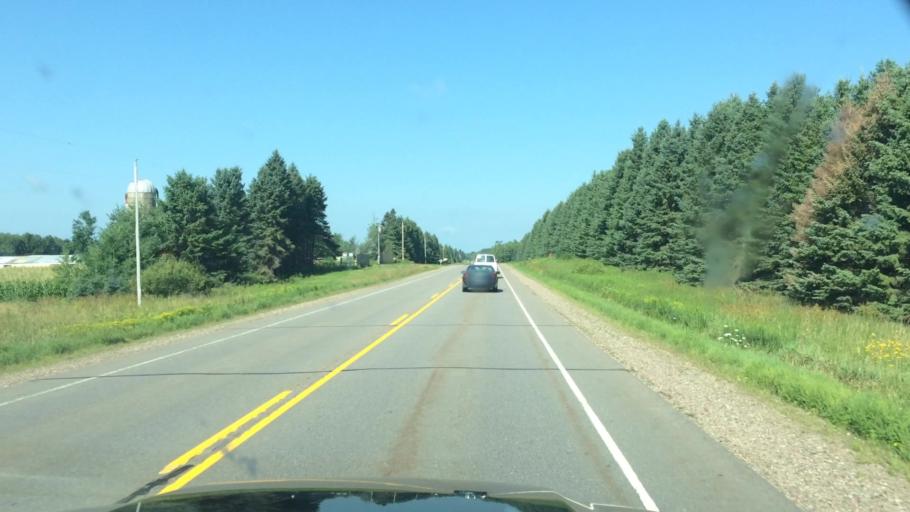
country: US
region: Wisconsin
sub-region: Lincoln County
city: Merrill
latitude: 45.1482
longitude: -89.4284
